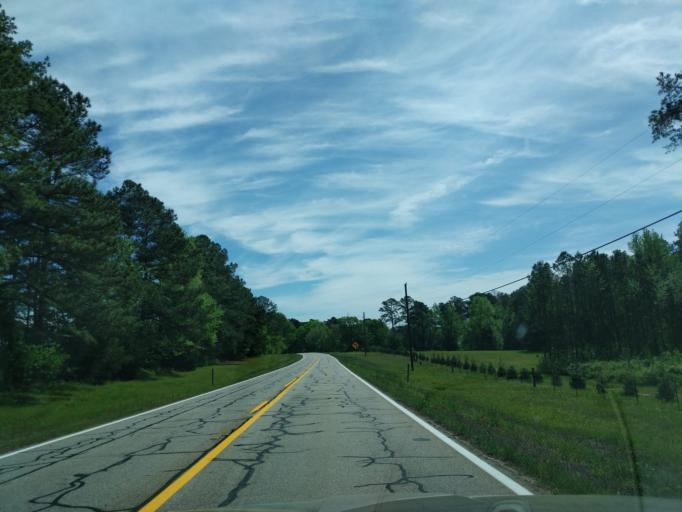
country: US
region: Georgia
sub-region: Columbia County
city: Appling
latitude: 33.6106
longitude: -82.3341
